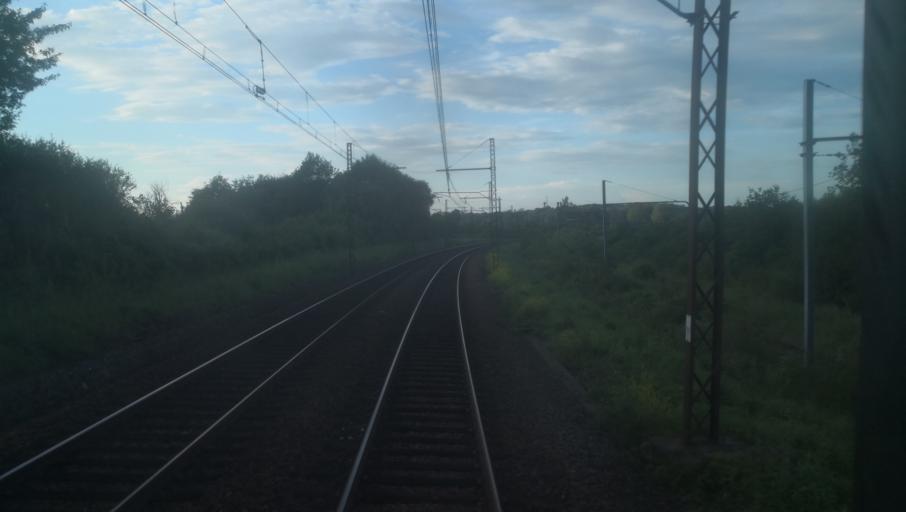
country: FR
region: Centre
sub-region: Departement de l'Indre
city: Argenton-sur-Creuse
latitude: 46.5116
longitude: 1.4986
